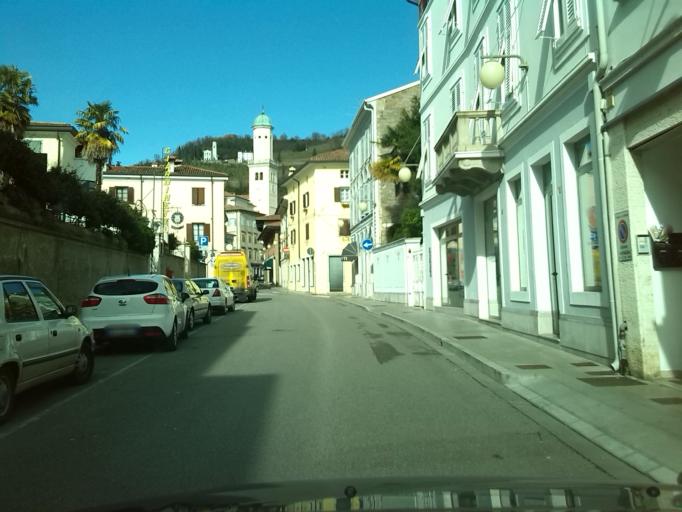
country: IT
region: Friuli Venezia Giulia
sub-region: Provincia di Gorizia
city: Cormons
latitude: 45.9592
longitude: 13.4724
